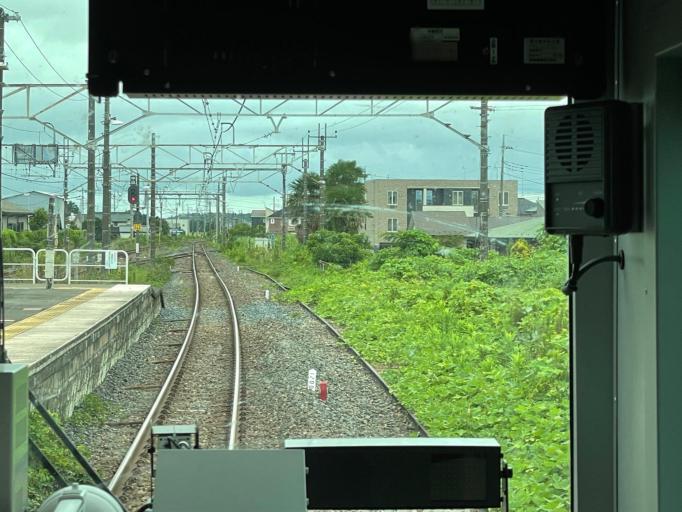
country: JP
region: Tochigi
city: Ujiie
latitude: 36.6810
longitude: 139.9623
